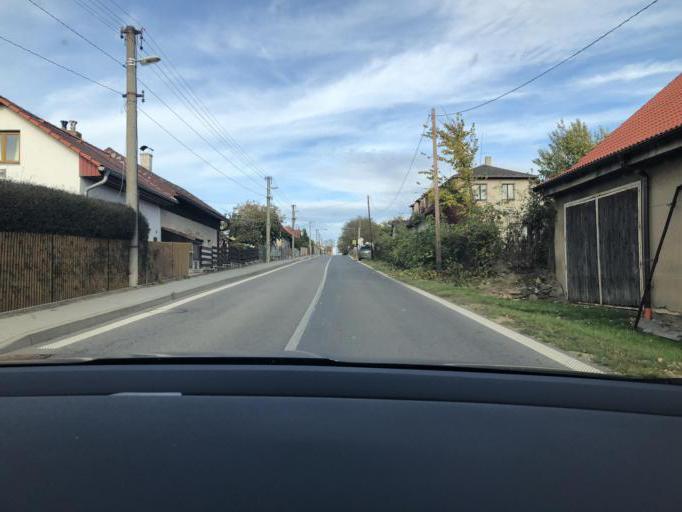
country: CZ
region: Central Bohemia
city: Divisov
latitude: 49.7927
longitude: 14.8816
